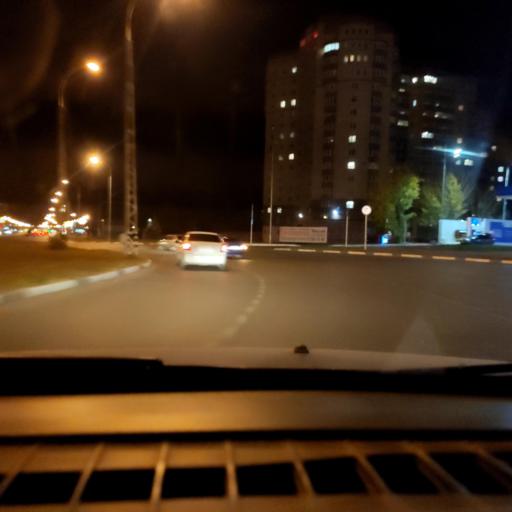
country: RU
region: Samara
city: Tol'yatti
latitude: 53.5394
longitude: 49.3602
